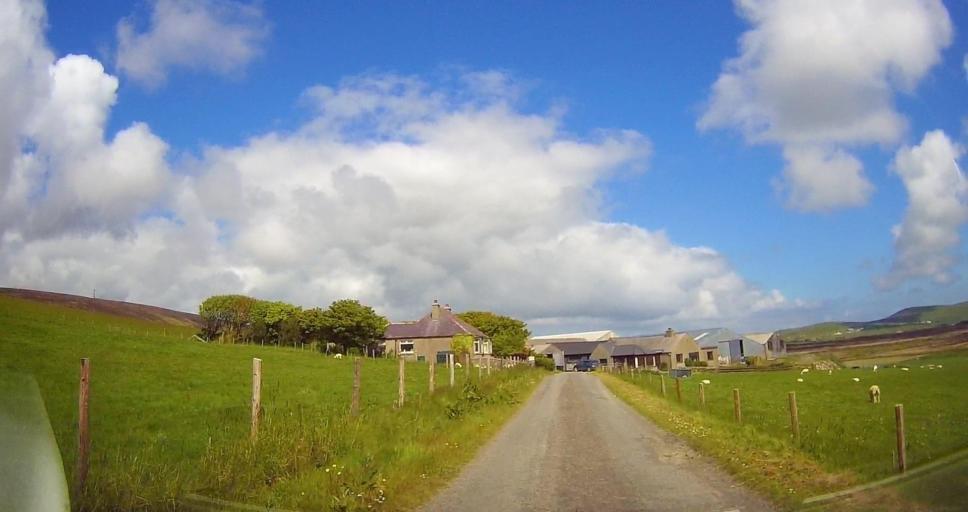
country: GB
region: Scotland
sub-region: Orkney Islands
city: Orkney
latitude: 59.0563
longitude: -3.1016
